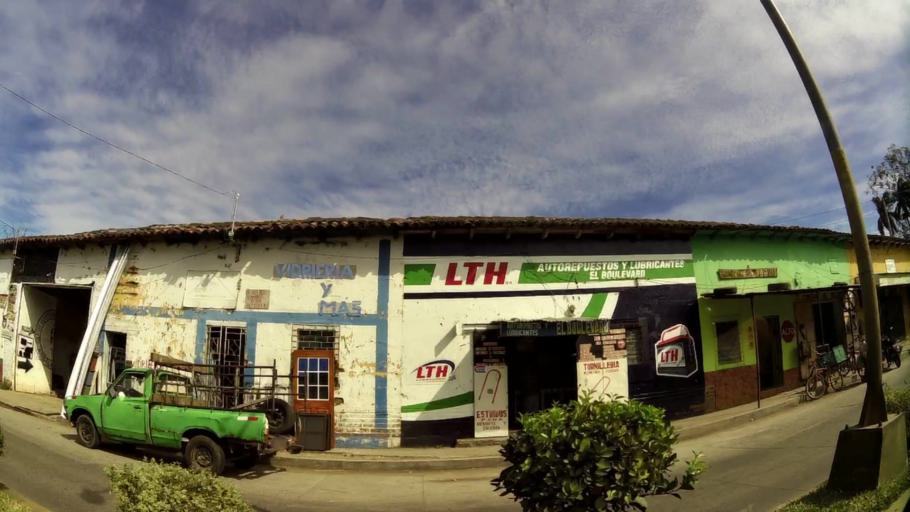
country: SV
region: Santa Ana
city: Chalchuapa
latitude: 13.9819
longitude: -89.6762
